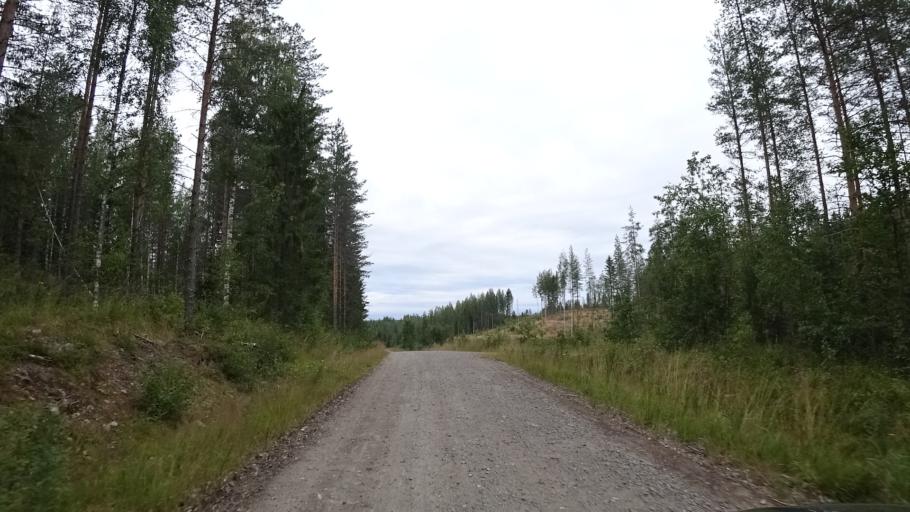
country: FI
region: North Karelia
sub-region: Joensuu
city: Ilomantsi
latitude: 63.1515
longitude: 30.6468
